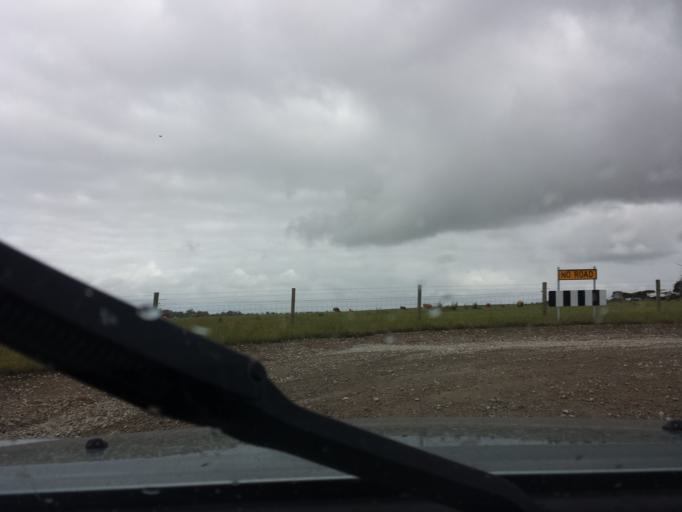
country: AU
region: Victoria
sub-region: Cardinia
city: Pakenham South
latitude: -38.0996
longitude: 145.4800
